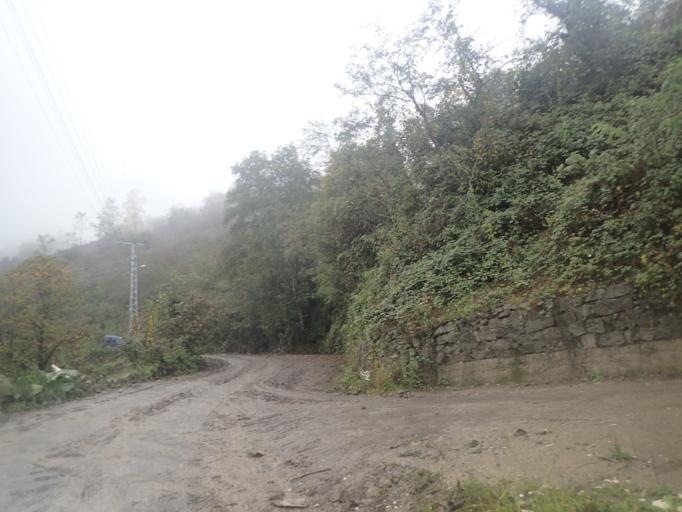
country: TR
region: Ordu
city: Persembe
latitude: 41.0372
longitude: 37.7196
